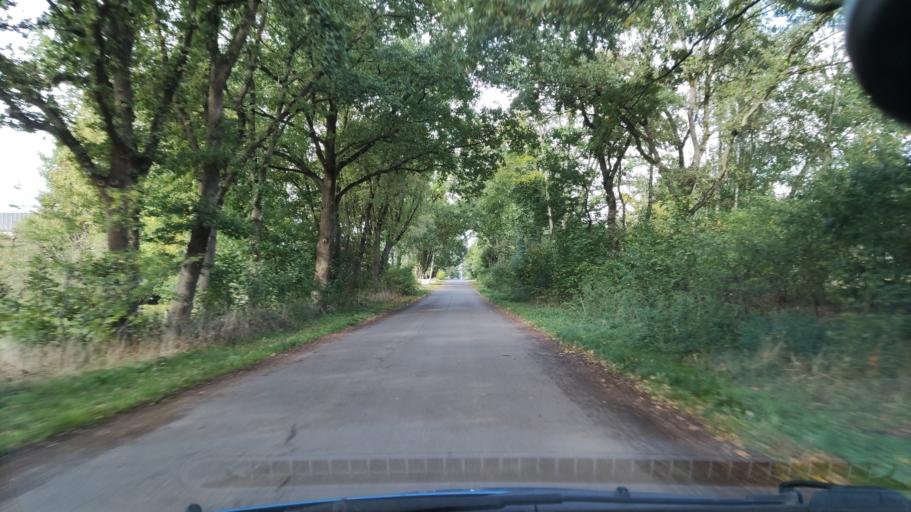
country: DE
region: Lower Saxony
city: Deutsch Evern
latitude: 53.2023
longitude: 10.4503
